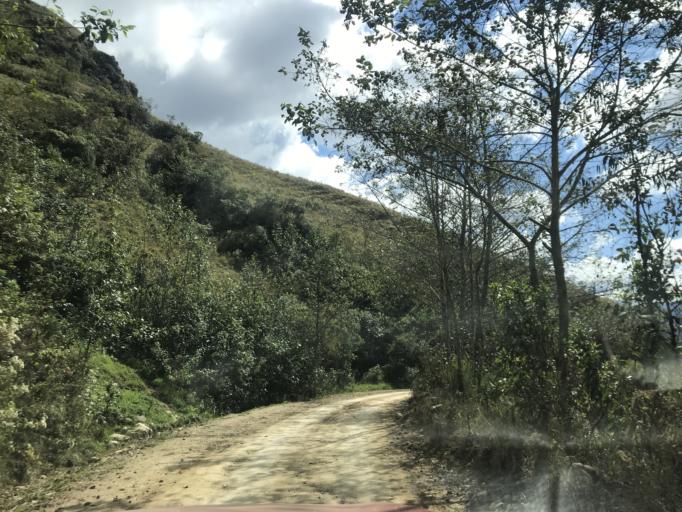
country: PE
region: Cajamarca
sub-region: Provincia de Chota
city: Querocoto
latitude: -6.3345
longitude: -79.0743
